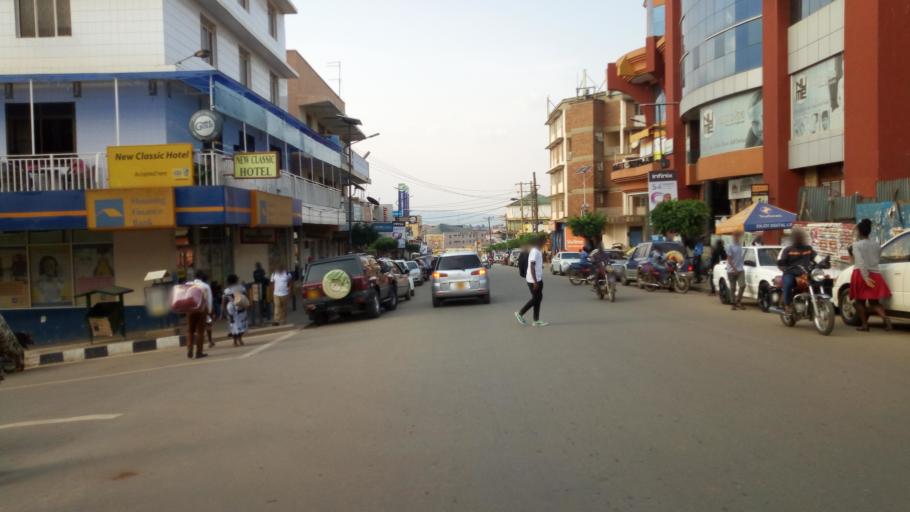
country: UG
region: Western Region
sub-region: Mbarara District
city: Mbarara
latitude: -0.6057
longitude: 30.6621
